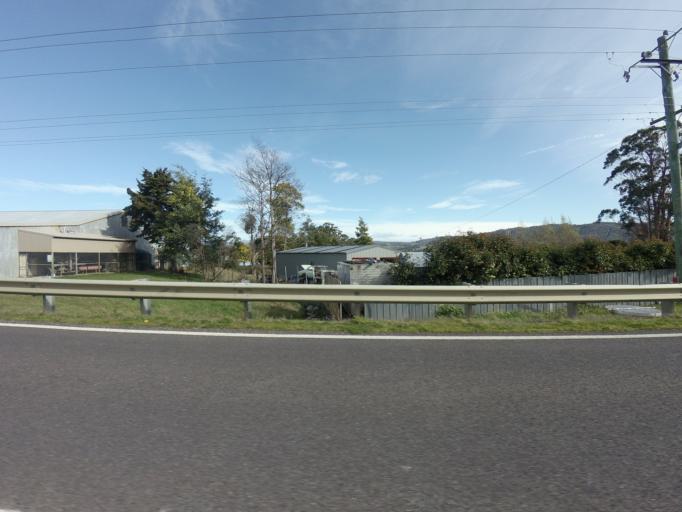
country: AU
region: Tasmania
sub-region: Huon Valley
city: Franklin
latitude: -43.1071
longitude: 147.0348
